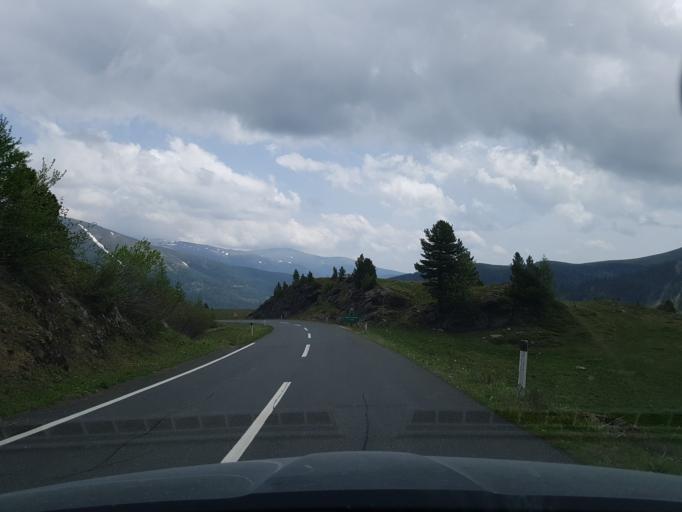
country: AT
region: Carinthia
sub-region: Politischer Bezirk Spittal an der Drau
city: Kleinkirchheim
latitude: 46.8867
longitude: 13.8008
